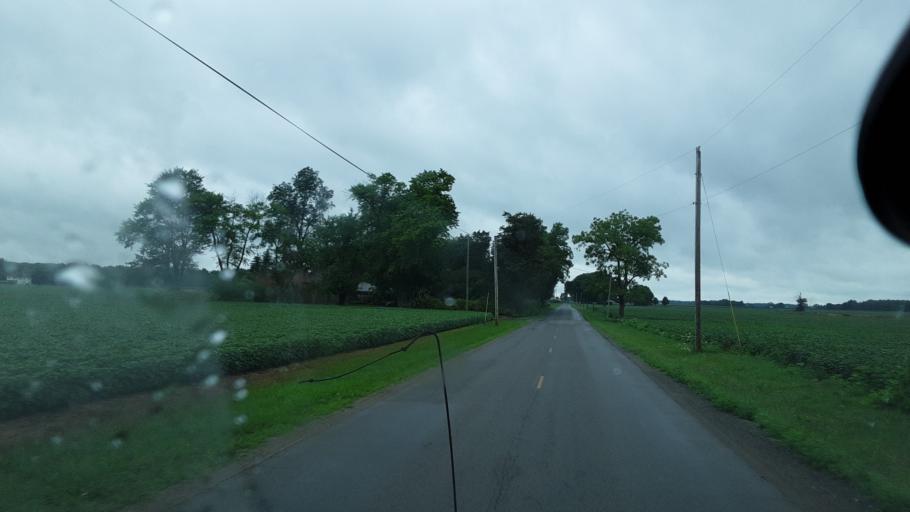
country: US
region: Ohio
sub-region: Van Wert County
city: Van Wert
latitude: 40.8005
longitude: -84.6228
